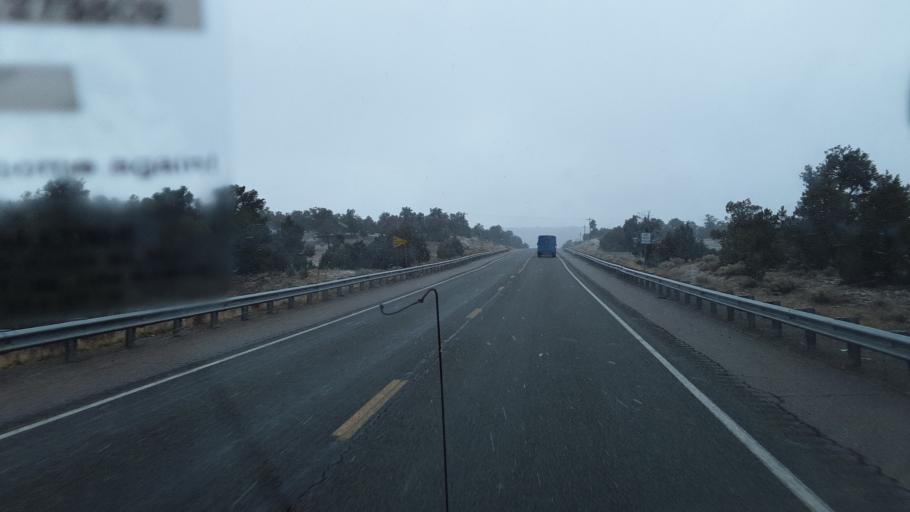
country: US
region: New Mexico
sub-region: Rio Arriba County
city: Tierra Amarilla
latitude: 36.4818
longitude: -106.4935
